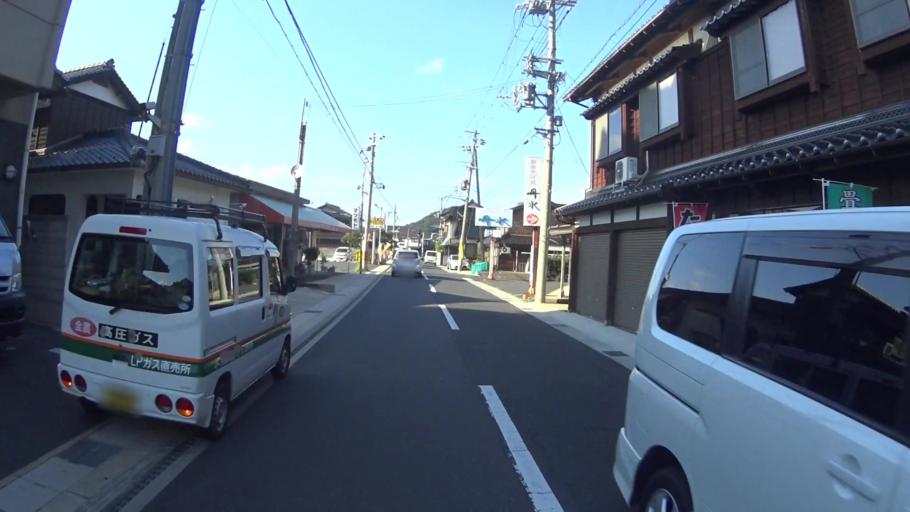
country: JP
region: Hyogo
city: Toyooka
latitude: 35.6614
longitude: 134.9688
